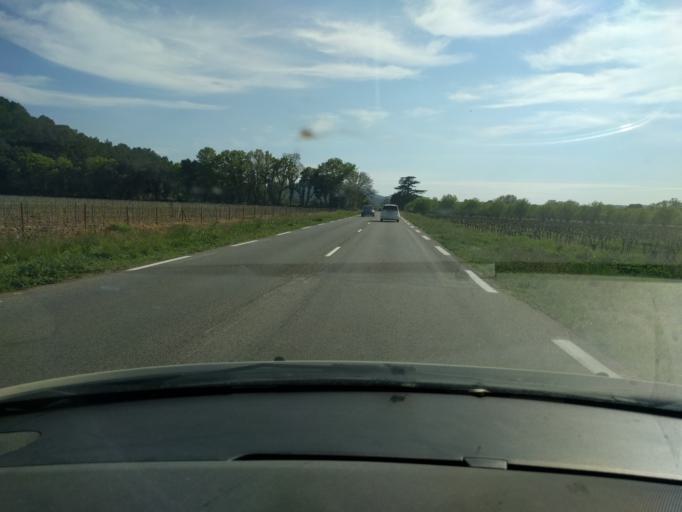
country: FR
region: Provence-Alpes-Cote d'Azur
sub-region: Departement du Var
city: Pierrefeu-du-Var
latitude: 43.1874
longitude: 6.1222
